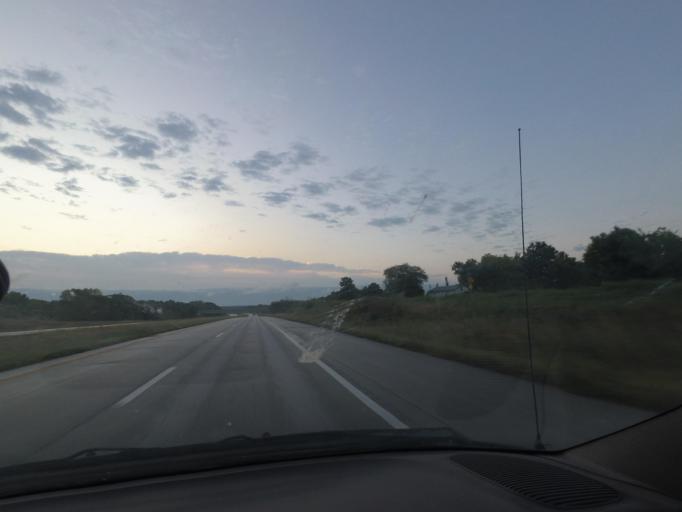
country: US
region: Missouri
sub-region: Macon County
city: Macon
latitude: 39.7526
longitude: -92.5335
